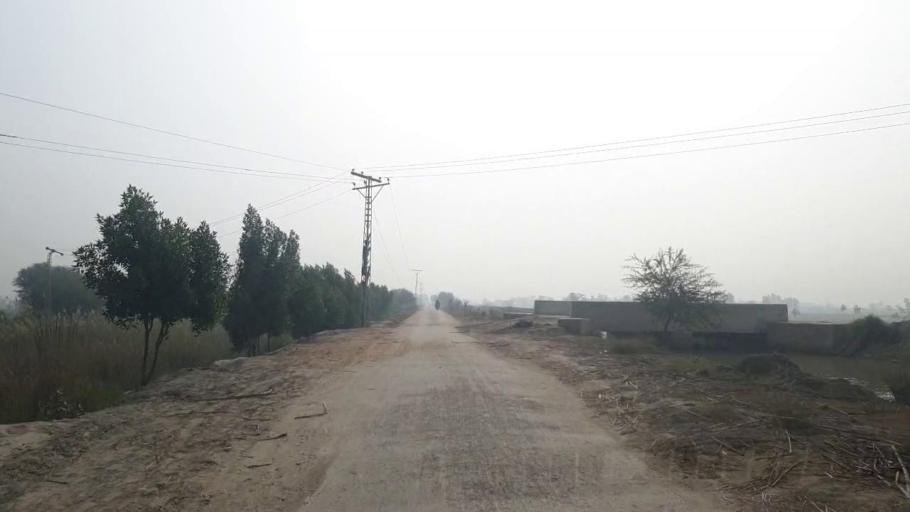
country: PK
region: Sindh
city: Tando Adam
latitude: 25.7612
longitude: 68.6114
